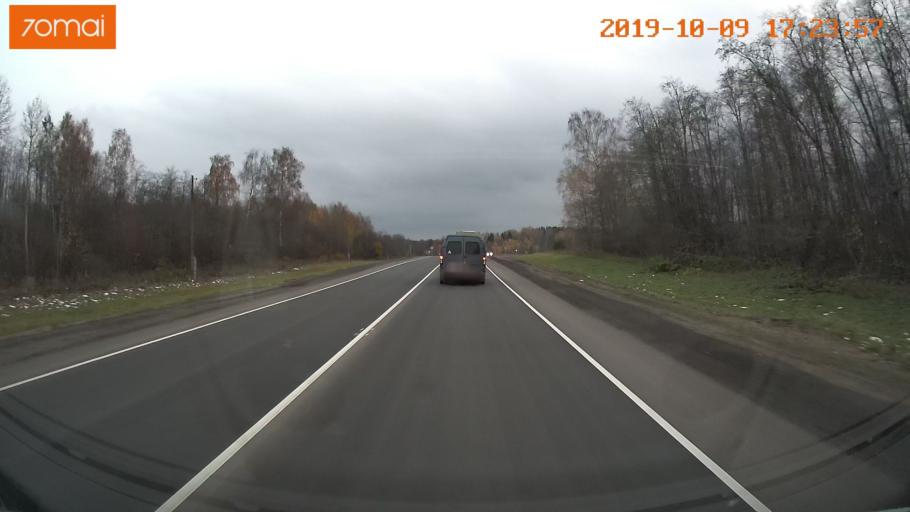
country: RU
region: Ivanovo
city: Furmanov
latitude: 57.1896
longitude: 41.1124
